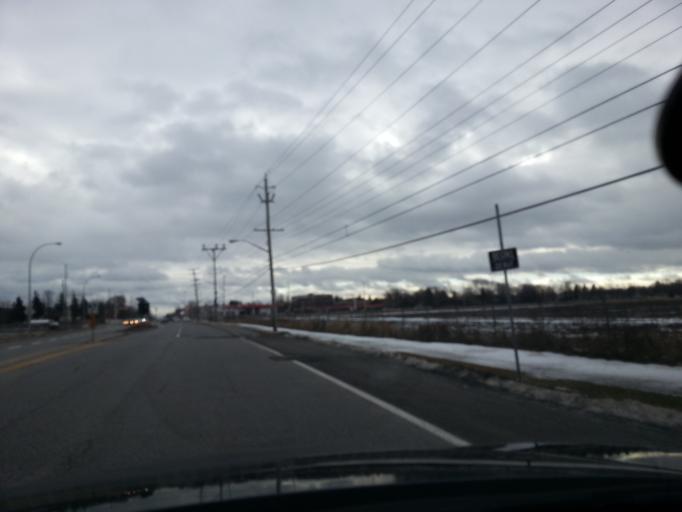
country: CA
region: Ontario
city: Bells Corners
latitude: 45.2901
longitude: -75.7582
